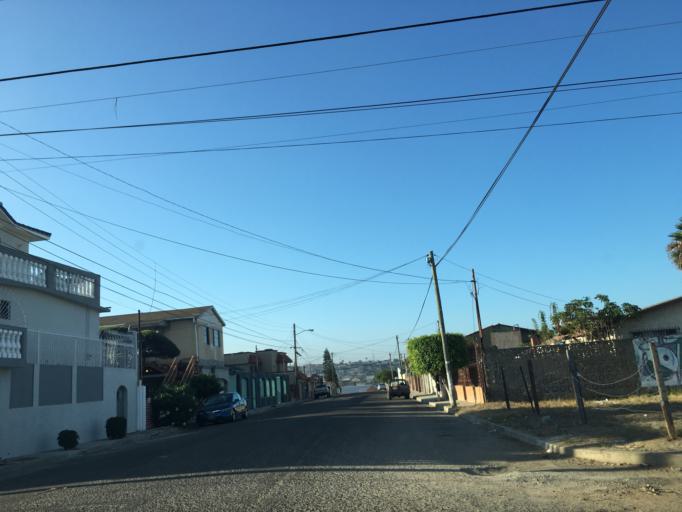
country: US
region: California
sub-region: San Diego County
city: Imperial Beach
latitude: 32.5335
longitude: -117.0782
